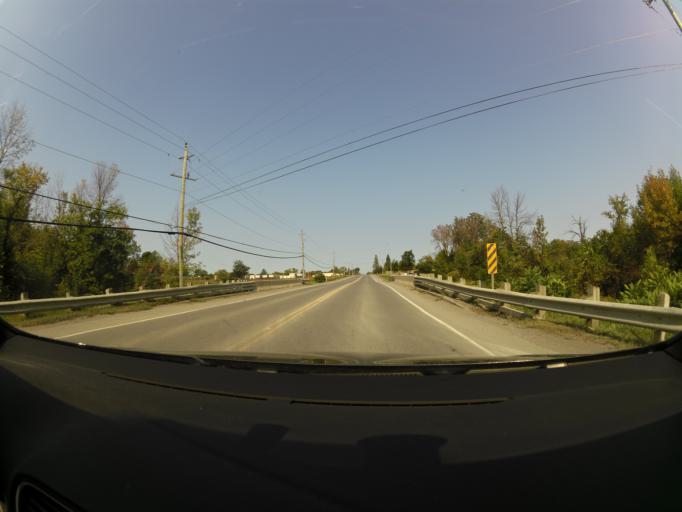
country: CA
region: Ontario
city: Bells Corners
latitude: 45.2994
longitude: -75.9797
